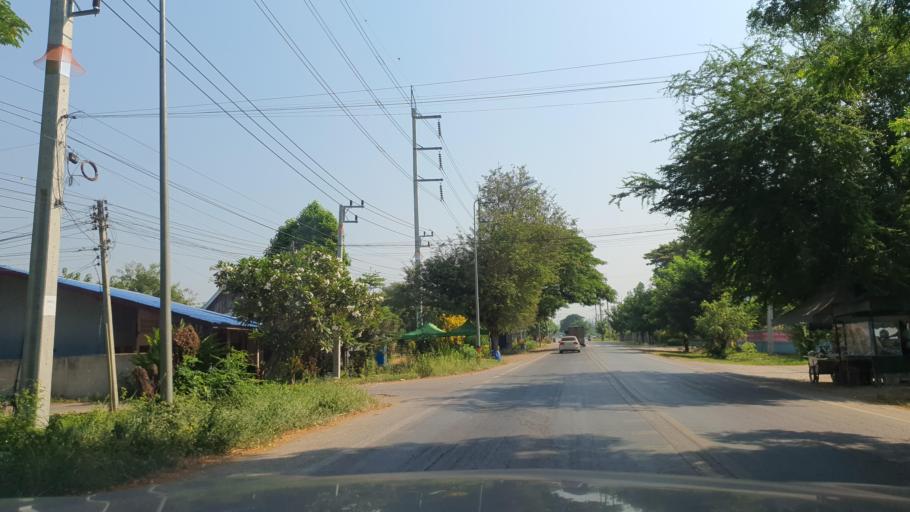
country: TH
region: Kanchanaburi
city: Kanchanaburi
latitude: 14.0541
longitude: 99.4743
